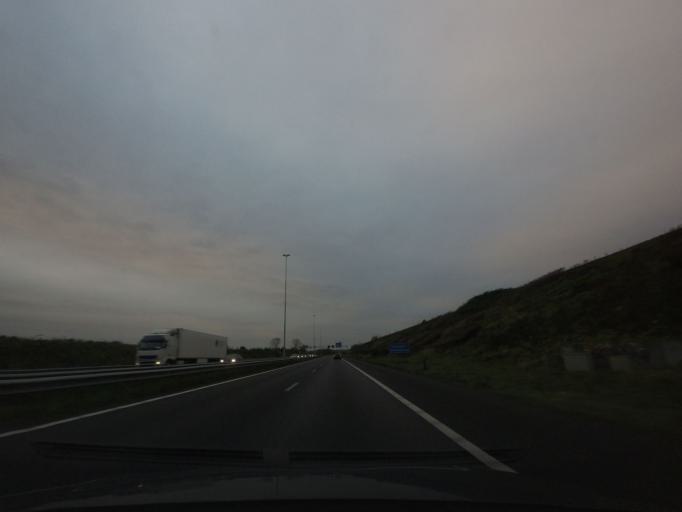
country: NL
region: North Brabant
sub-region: Gemeente Breda
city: Breda
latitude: 51.5646
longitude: 4.8207
